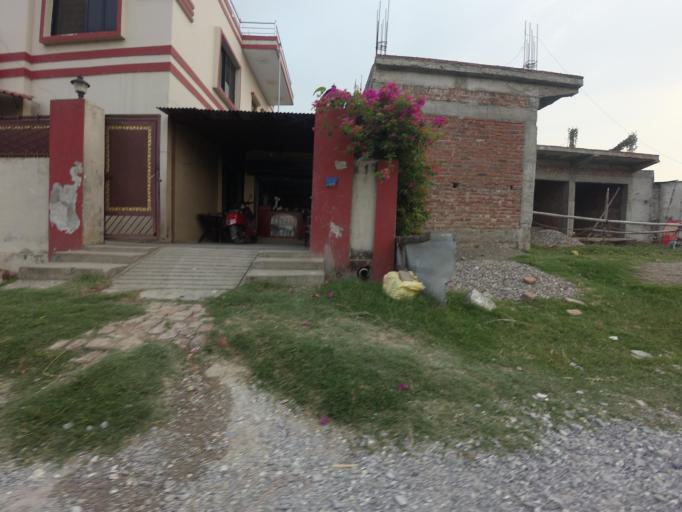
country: NP
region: Western Region
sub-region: Lumbini Zone
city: Bhairahawa
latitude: 27.4981
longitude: 83.4445
